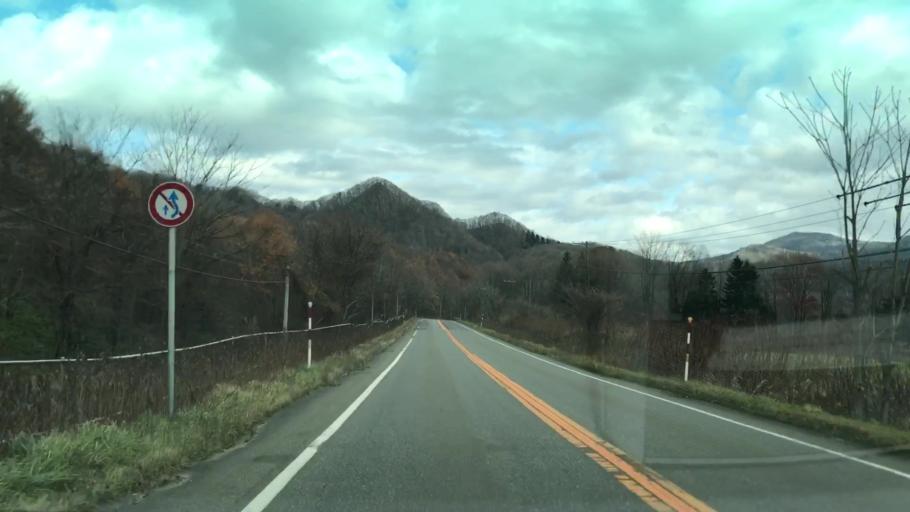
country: JP
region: Hokkaido
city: Shizunai-furukawacho
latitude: 42.8093
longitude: 142.4029
